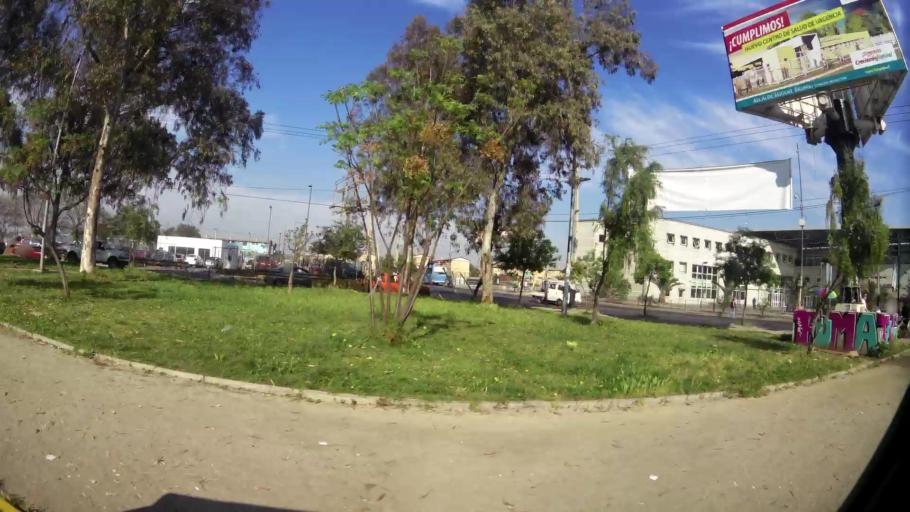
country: CL
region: Santiago Metropolitan
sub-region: Provincia de Maipo
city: San Bernardo
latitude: -33.5229
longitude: -70.6977
